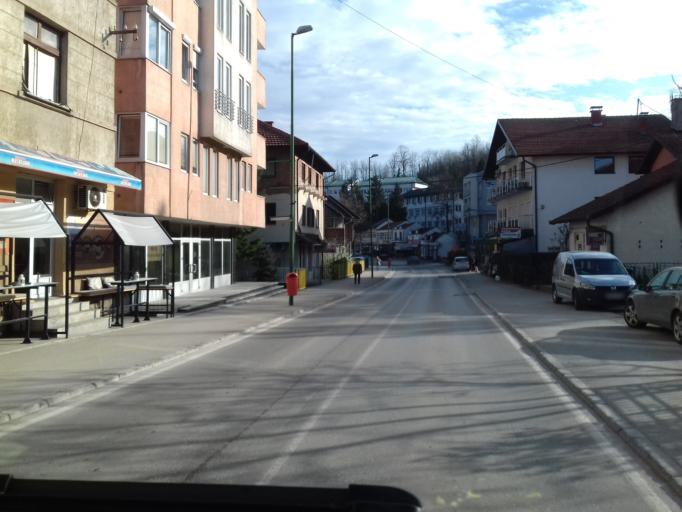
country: BA
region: Federation of Bosnia and Herzegovina
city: Tesanj
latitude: 44.6076
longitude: 17.9875
